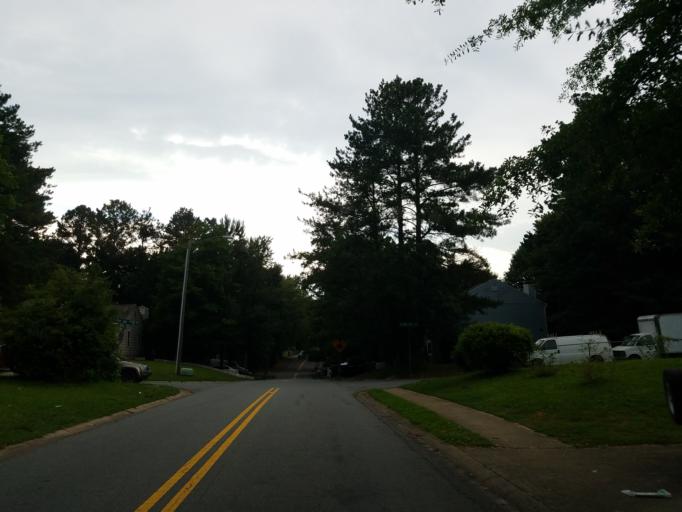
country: US
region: Georgia
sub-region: Cobb County
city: Fair Oaks
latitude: 33.9221
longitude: -84.5604
